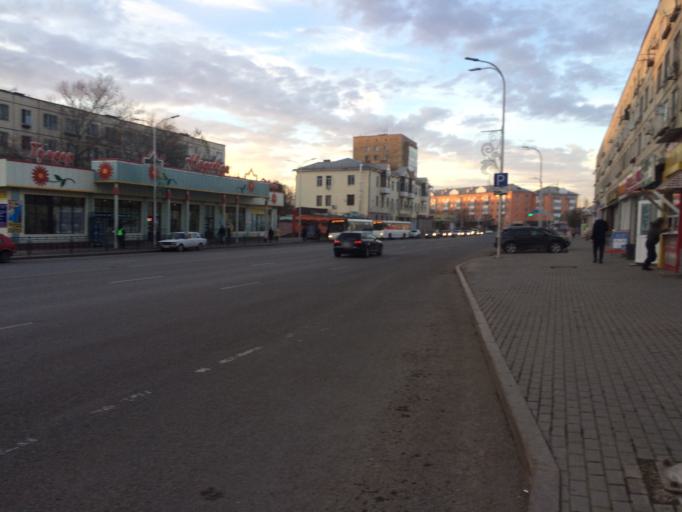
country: KZ
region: Astana Qalasy
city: Astana
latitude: 51.1868
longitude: 71.4158
